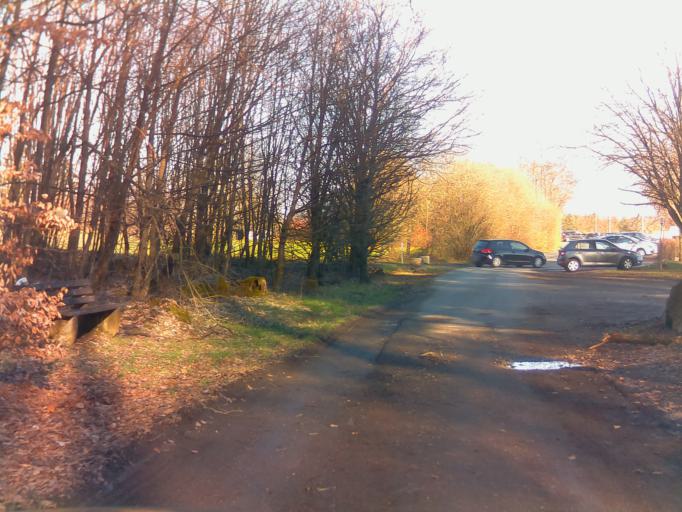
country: DE
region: Rheinland-Pfalz
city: Siesbach
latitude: 49.7529
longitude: 7.2270
